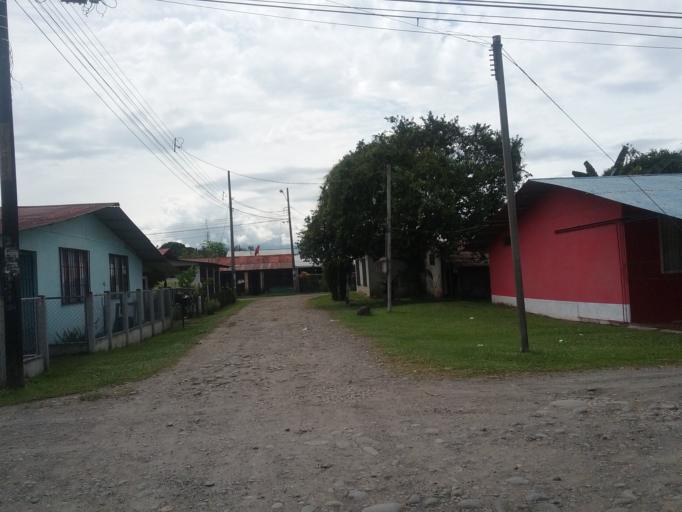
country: CR
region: Limon
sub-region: Canton de Pococi
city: Guapiles
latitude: 10.3194
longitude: -83.8864
